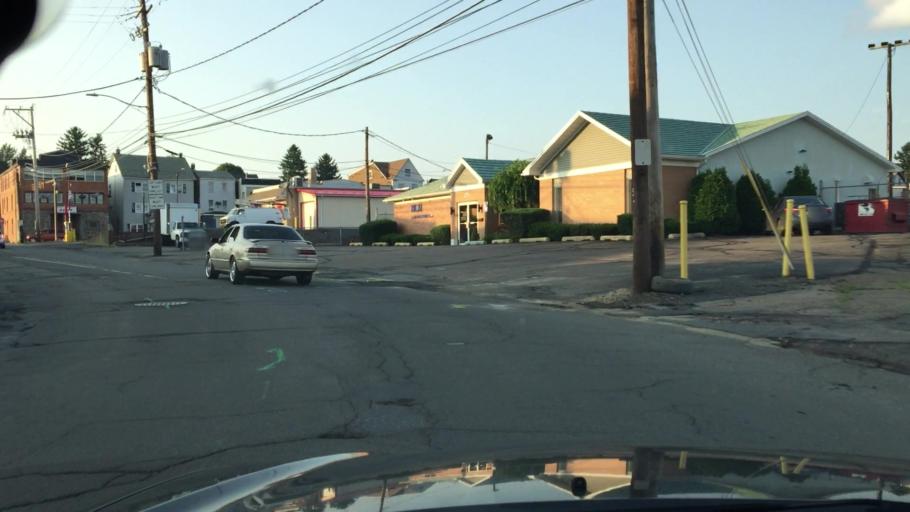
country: US
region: Pennsylvania
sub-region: Luzerne County
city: Hazleton
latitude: 40.9601
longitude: -75.9676
